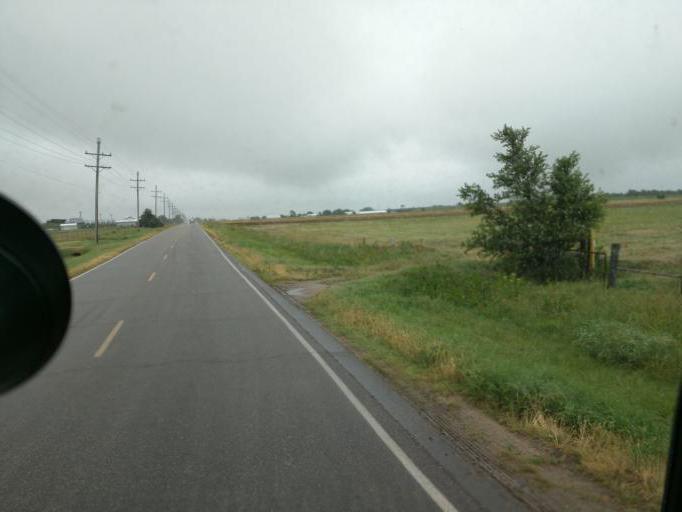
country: US
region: Kansas
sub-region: Reno County
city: Haven
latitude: 37.9335
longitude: -97.8852
